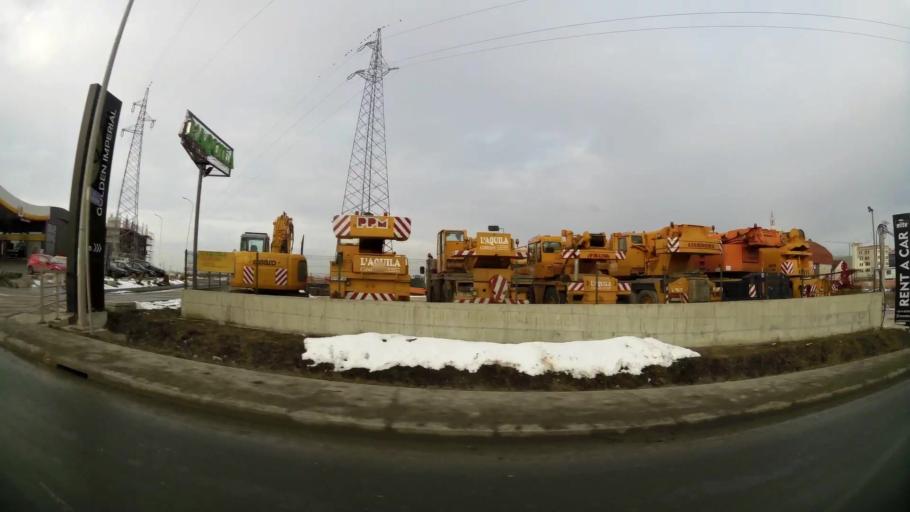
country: XK
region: Pristina
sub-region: Komuna e Prishtines
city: Pristina
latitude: 42.6315
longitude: 21.1462
